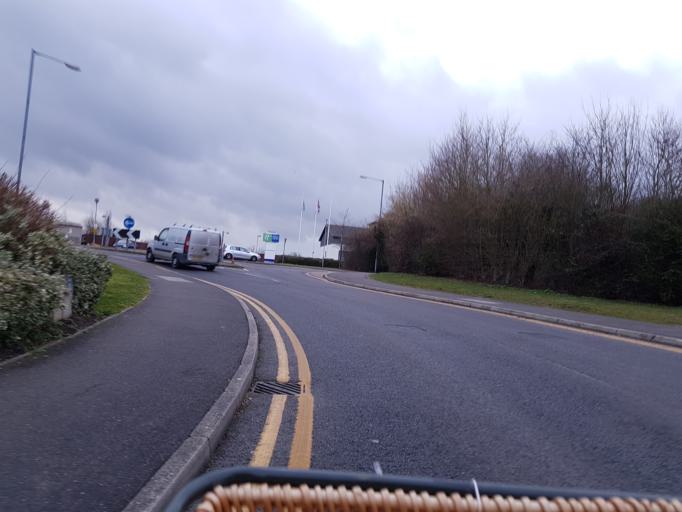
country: GB
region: England
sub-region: Cambridgeshire
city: Cambridge
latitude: 52.1950
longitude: 0.1665
